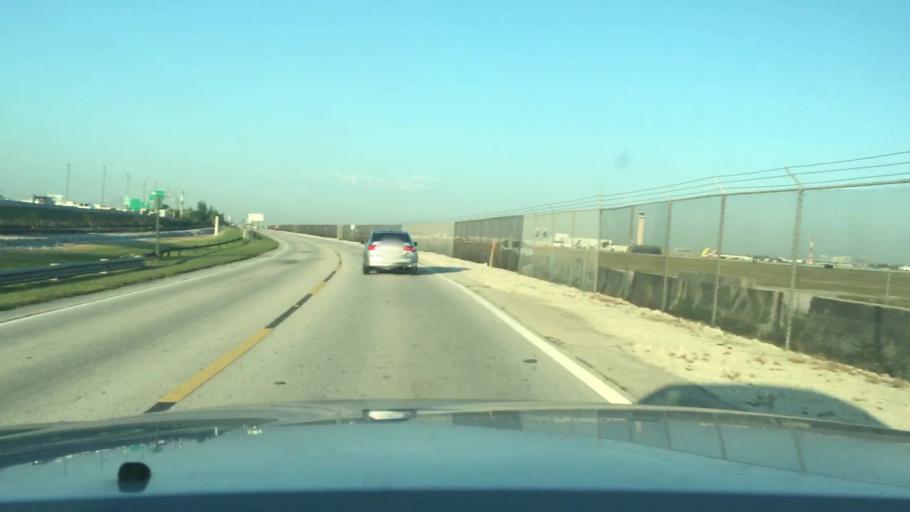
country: US
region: Florida
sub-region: Miami-Dade County
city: West Miami
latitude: 25.7859
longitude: -80.2791
